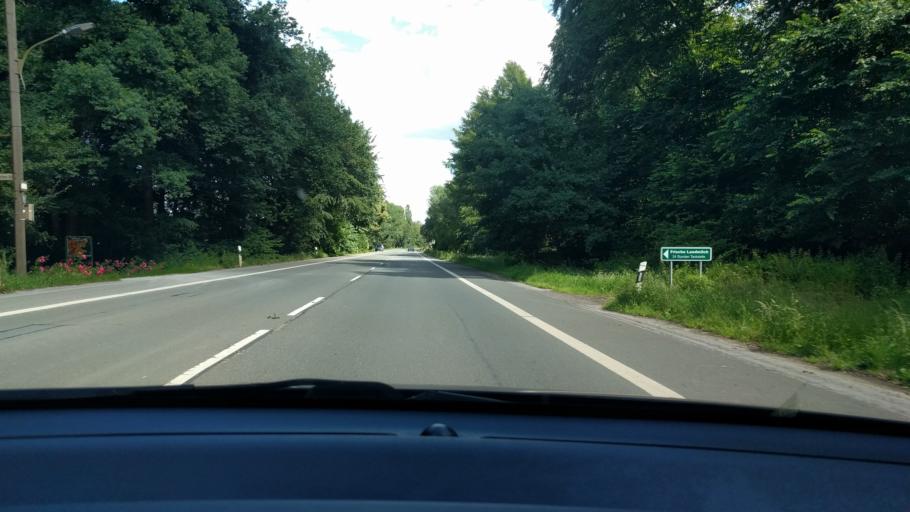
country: DE
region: North Rhine-Westphalia
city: Oer-Erkenschwick
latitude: 51.7145
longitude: 7.2730
